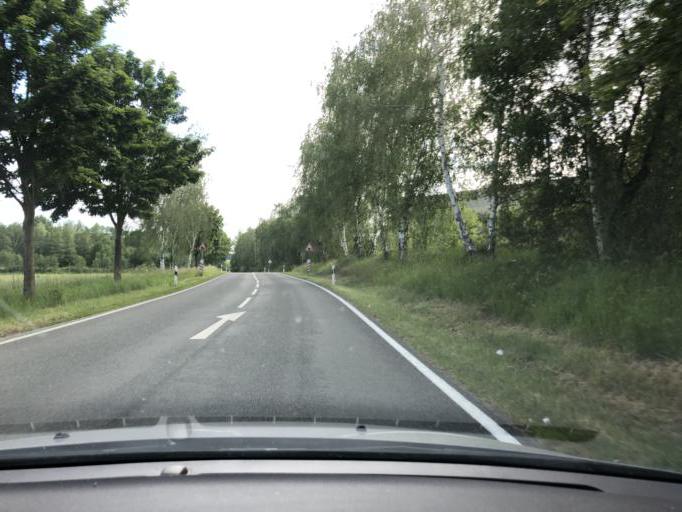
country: DE
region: Saxony
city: Trebsen
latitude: 51.2847
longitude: 12.7363
